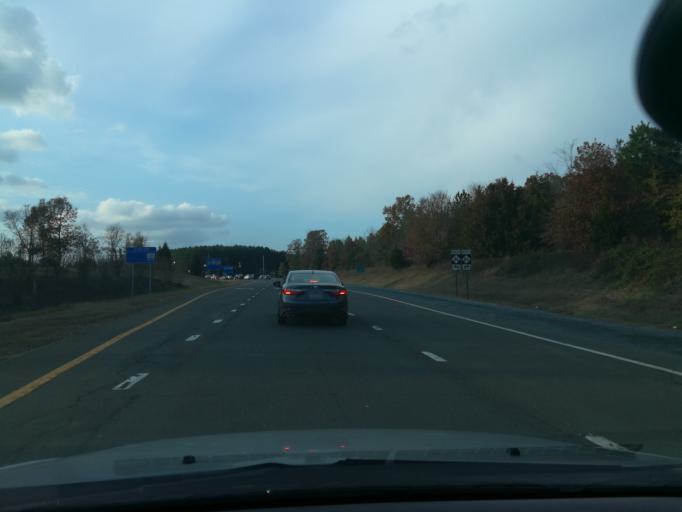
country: US
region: North Carolina
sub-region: Orange County
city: Chapel Hill
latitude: 35.9713
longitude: -79.0616
